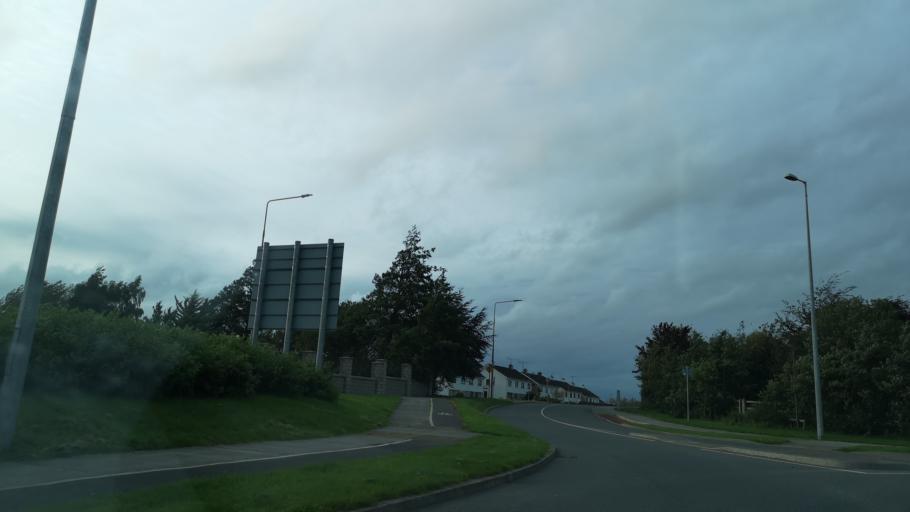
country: IE
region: Leinster
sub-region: An Iarmhi
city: Athlone
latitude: 53.4194
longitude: -7.9005
